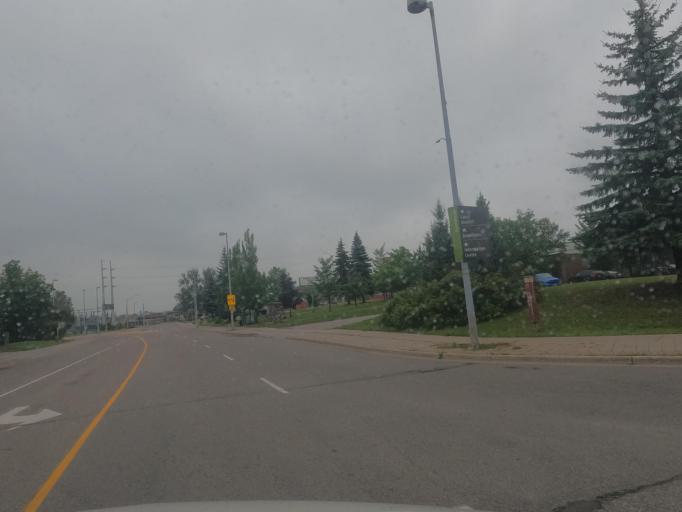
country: CA
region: Ontario
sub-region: Algoma
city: Sault Ste. Marie
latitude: 46.5183
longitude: -84.3480
